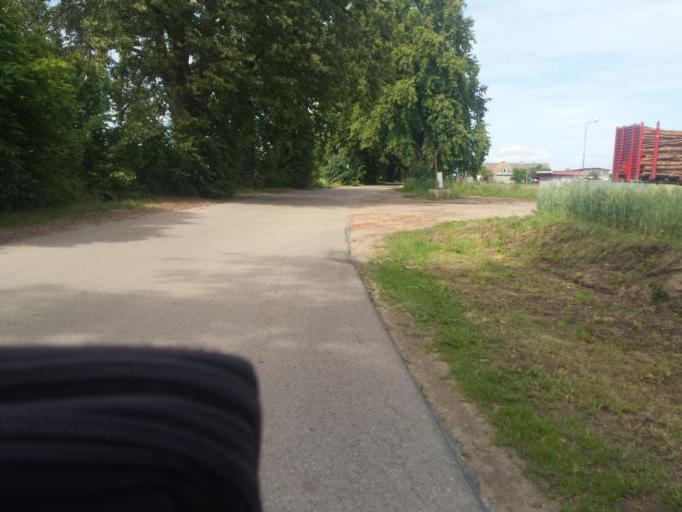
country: PL
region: Warmian-Masurian Voivodeship
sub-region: Powiat nowomiejski
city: Biskupiec
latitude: 53.5883
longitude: 19.4270
